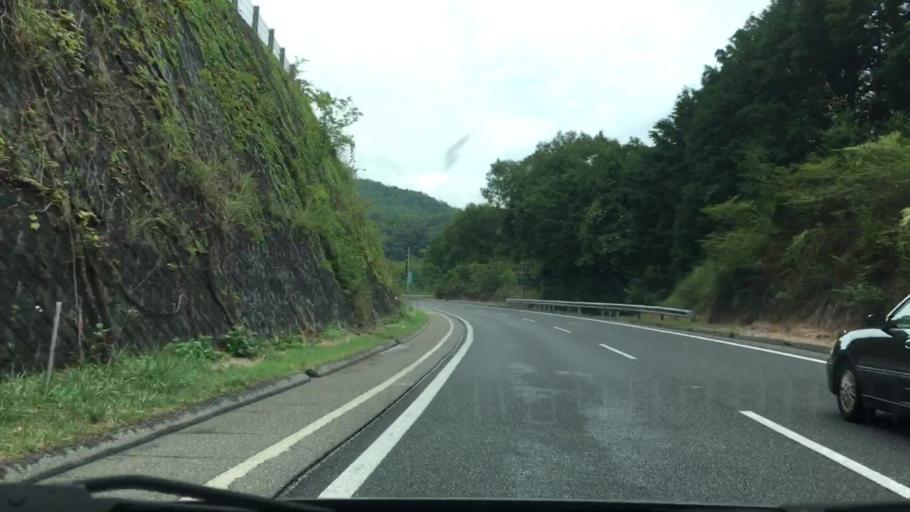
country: JP
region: Okayama
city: Niimi
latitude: 34.9899
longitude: 133.6065
